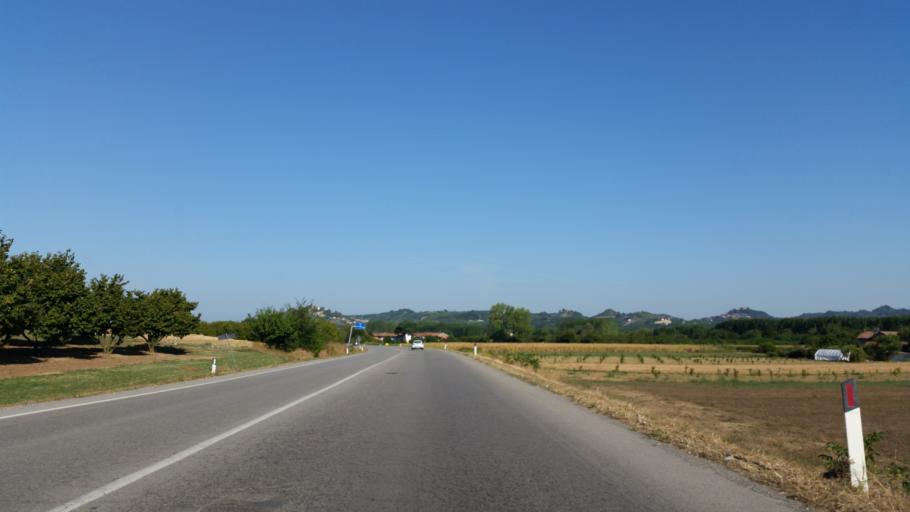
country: IT
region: Piedmont
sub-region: Provincia di Cuneo
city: Roddi
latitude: 44.6829
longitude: 7.9803
